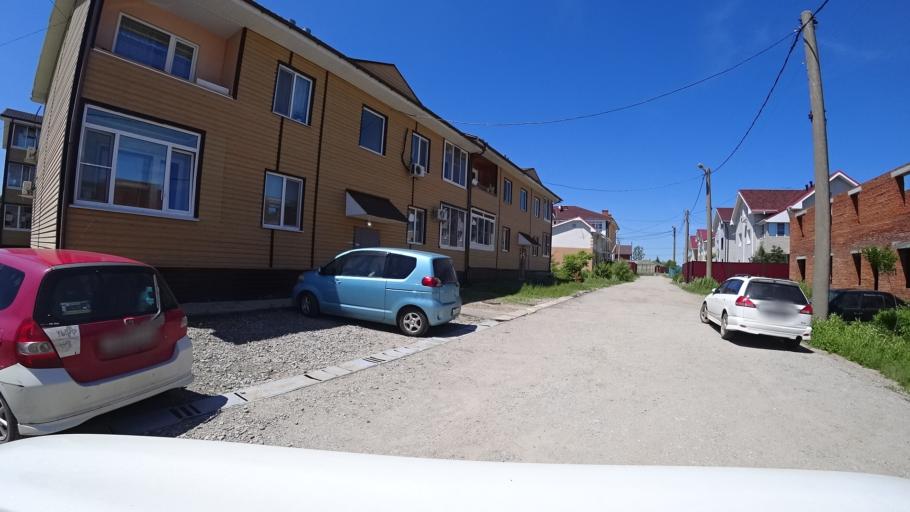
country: RU
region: Khabarovsk Krai
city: Topolevo
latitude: 48.5087
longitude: 135.1864
